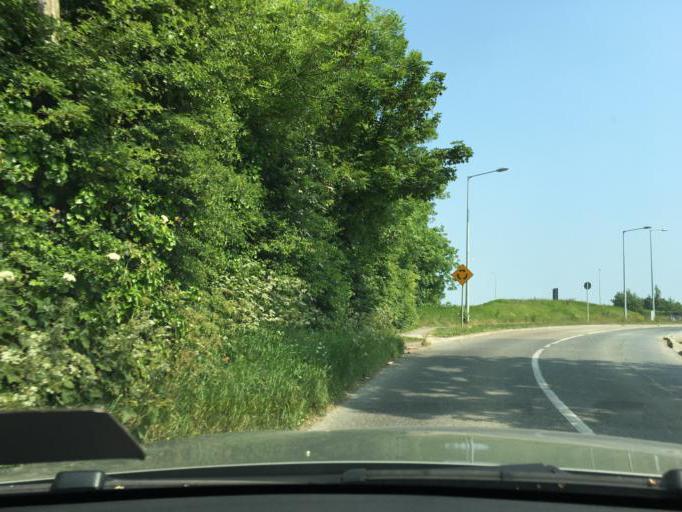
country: IE
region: Leinster
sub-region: Fingal County
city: Blanchardstown
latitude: 53.4146
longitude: -6.3884
